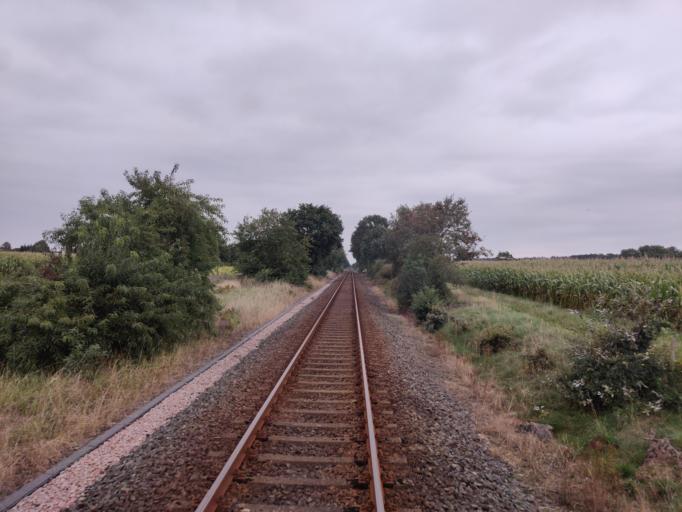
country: DE
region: Lower Saxony
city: Kutenholz
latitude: 53.4974
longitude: 9.3019
